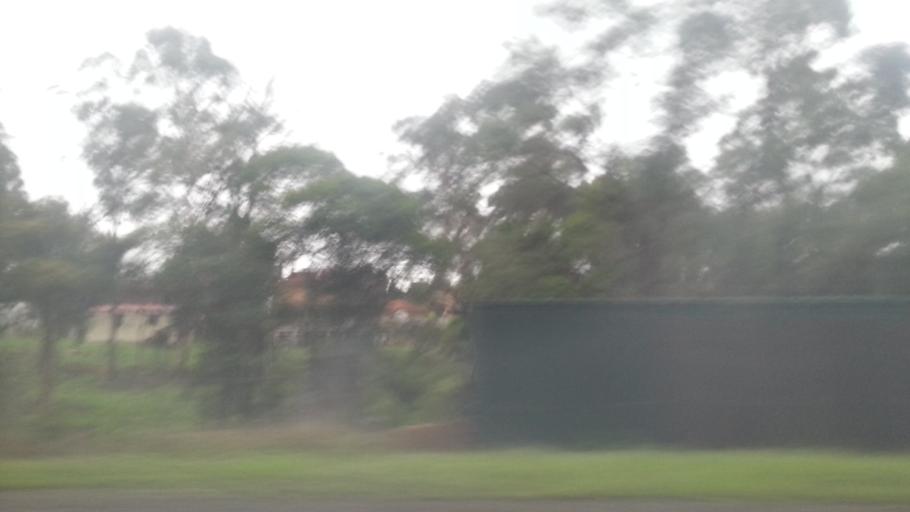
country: AU
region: New South Wales
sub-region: Wollondilly
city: Douglas Park
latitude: -34.1863
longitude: 150.7136
